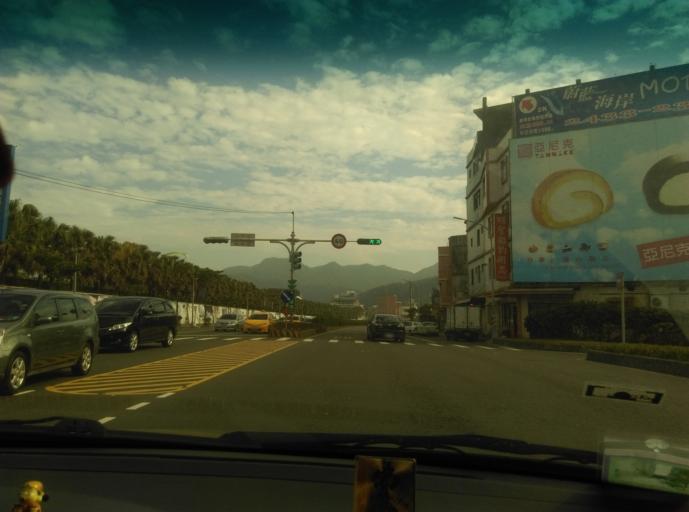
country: TW
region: Taiwan
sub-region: Keelung
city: Keelung
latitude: 25.1823
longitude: 121.6882
